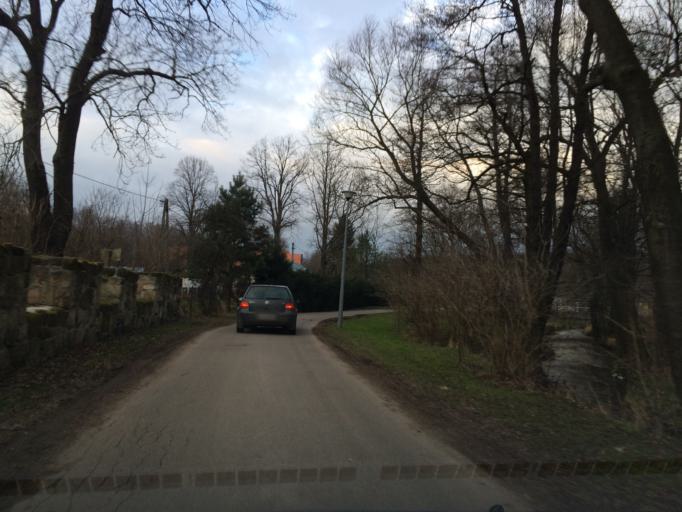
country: PL
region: Lower Silesian Voivodeship
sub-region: Powiat lwowecki
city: Lwowek Slaski
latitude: 51.0918
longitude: 15.5944
